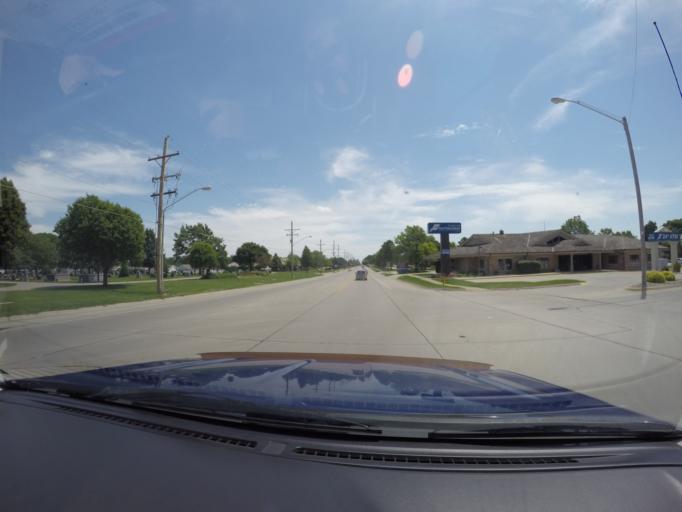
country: US
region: Nebraska
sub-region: Hall County
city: Grand Island
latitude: 40.9024
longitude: -98.3725
